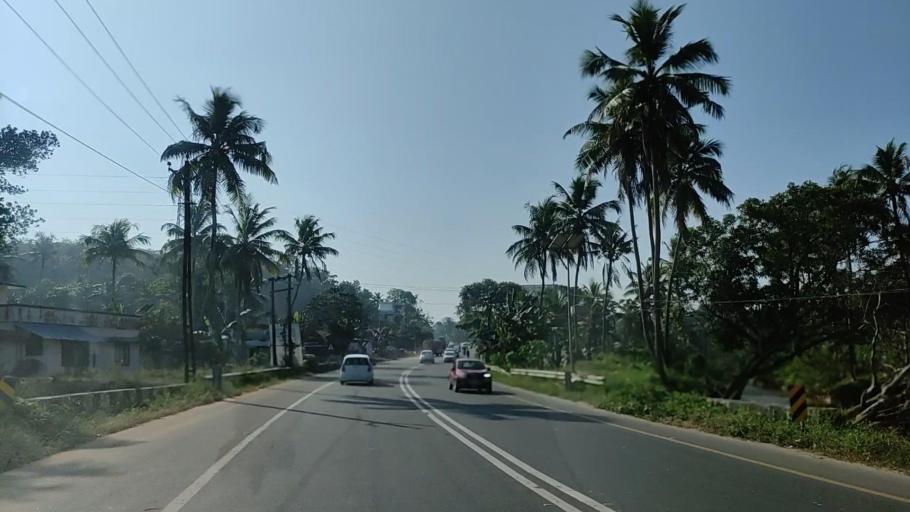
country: IN
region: Kerala
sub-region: Kollam
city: Punalur
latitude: 8.9049
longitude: 76.8556
